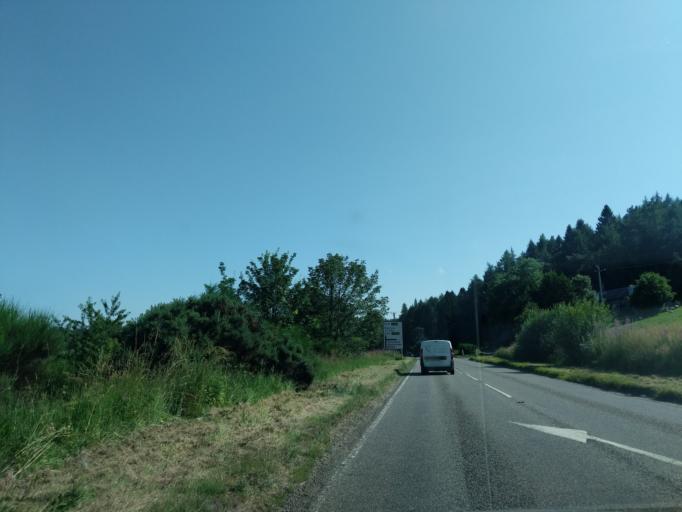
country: GB
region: Scotland
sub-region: Moray
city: Rothes
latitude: 57.5011
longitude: -3.1927
